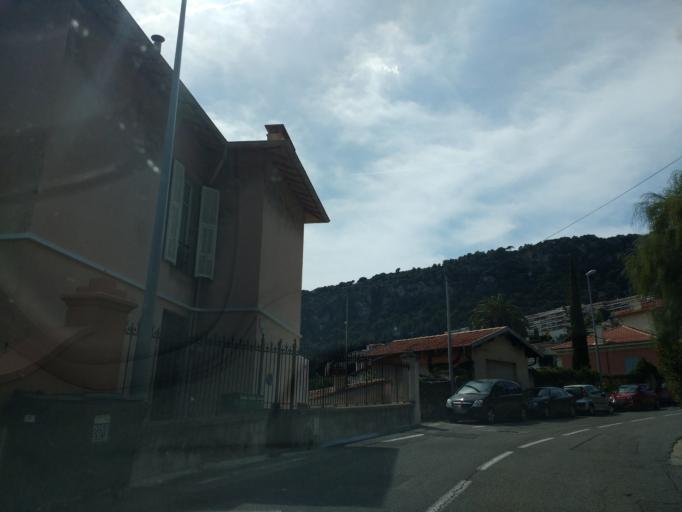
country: FR
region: Provence-Alpes-Cote d'Azur
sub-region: Departement des Alpes-Maritimes
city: Villefranche-sur-Mer
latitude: 43.7003
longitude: 7.3090
